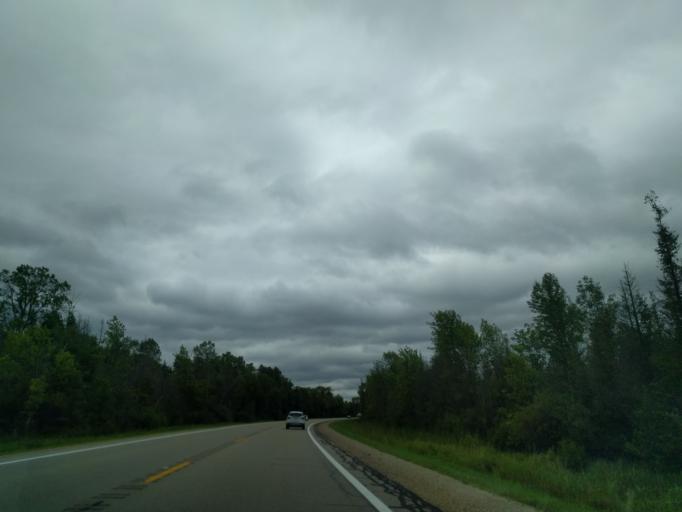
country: US
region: Michigan
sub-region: Menominee County
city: Menominee
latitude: 45.3812
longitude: -87.3764
